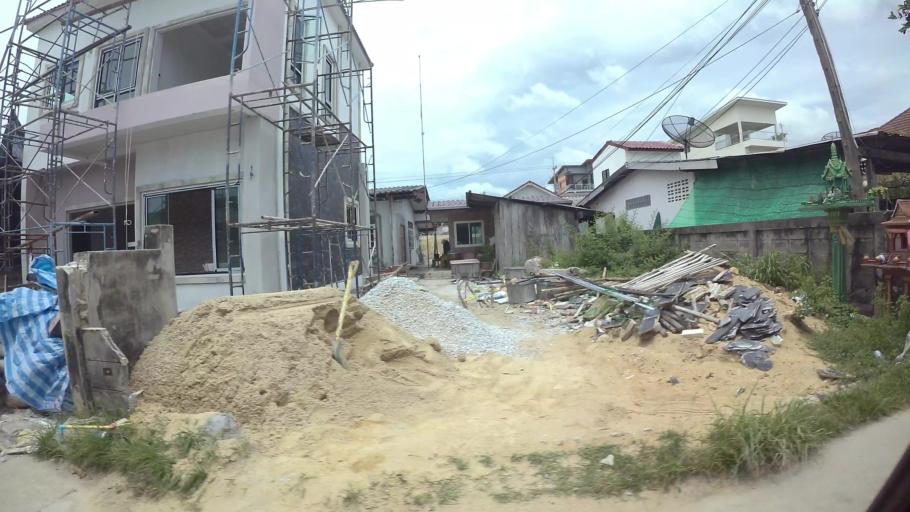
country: TH
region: Chon Buri
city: Sattahip
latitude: 12.7620
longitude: 100.8869
